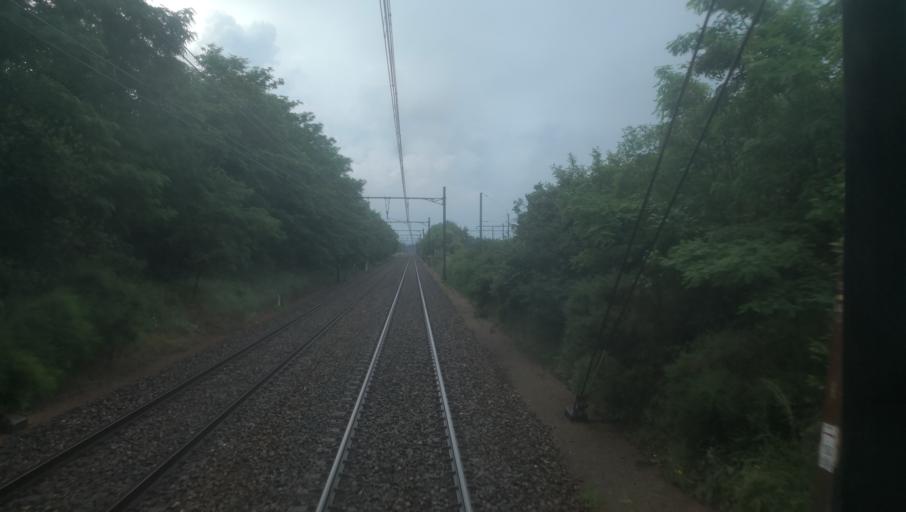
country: FR
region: Centre
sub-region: Departement du Loiret
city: Saint-Cyr-en-Val
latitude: 47.8095
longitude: 1.9456
